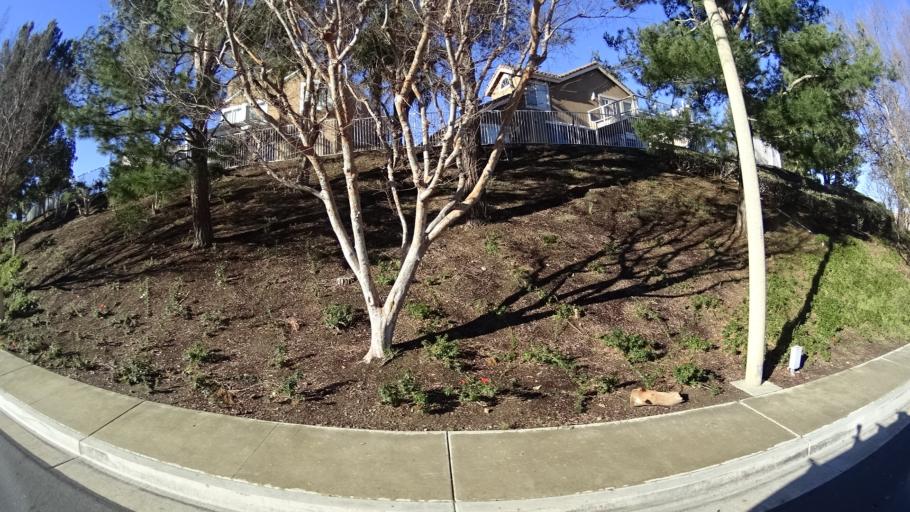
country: US
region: California
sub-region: Orange County
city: Yorba Linda
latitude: 33.8639
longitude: -117.7273
